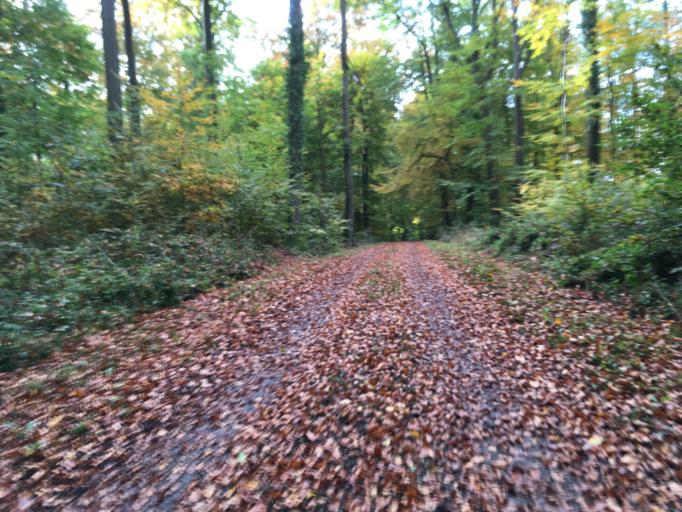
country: DE
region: Baden-Wuerttemberg
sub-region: Karlsruhe Region
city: Waibstadt
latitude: 49.2723
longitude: 8.9239
